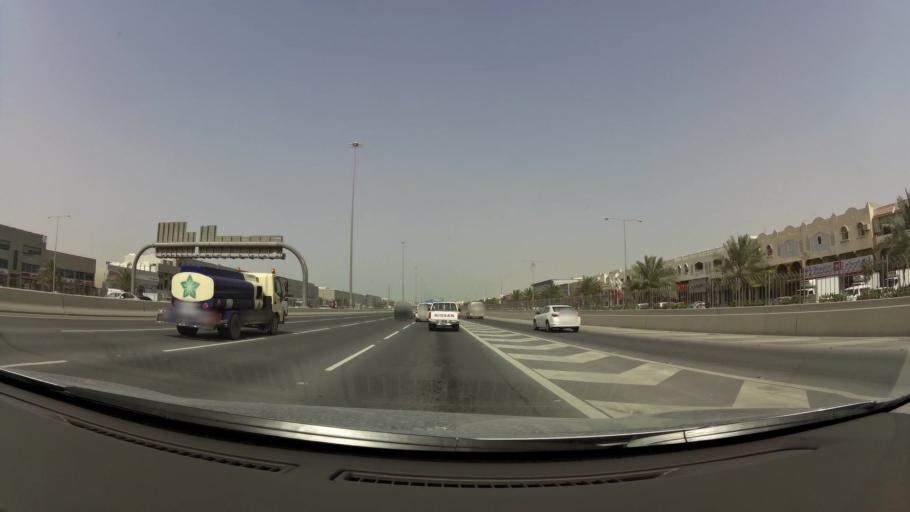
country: QA
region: Baladiyat ad Dawhah
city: Doha
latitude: 25.2516
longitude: 51.4763
